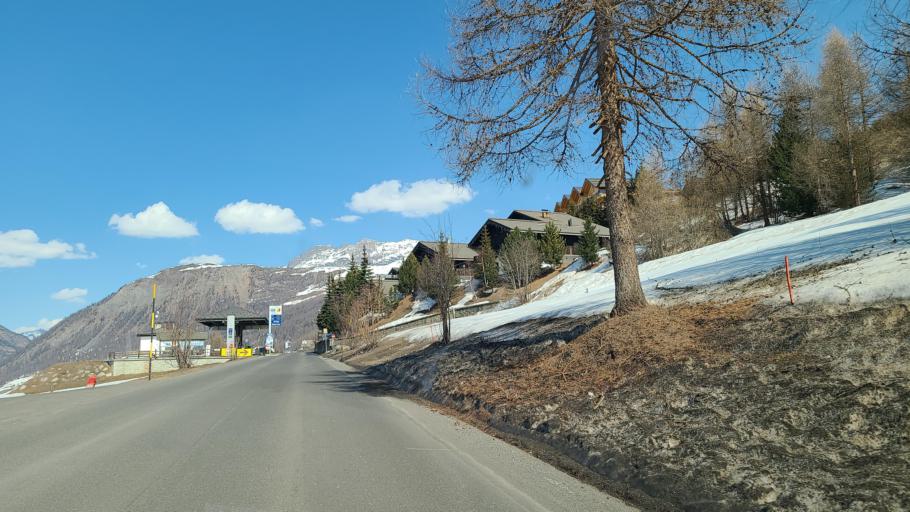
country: IT
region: Lombardy
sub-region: Provincia di Sondrio
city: Livigno
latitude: 46.5267
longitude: 10.1343
